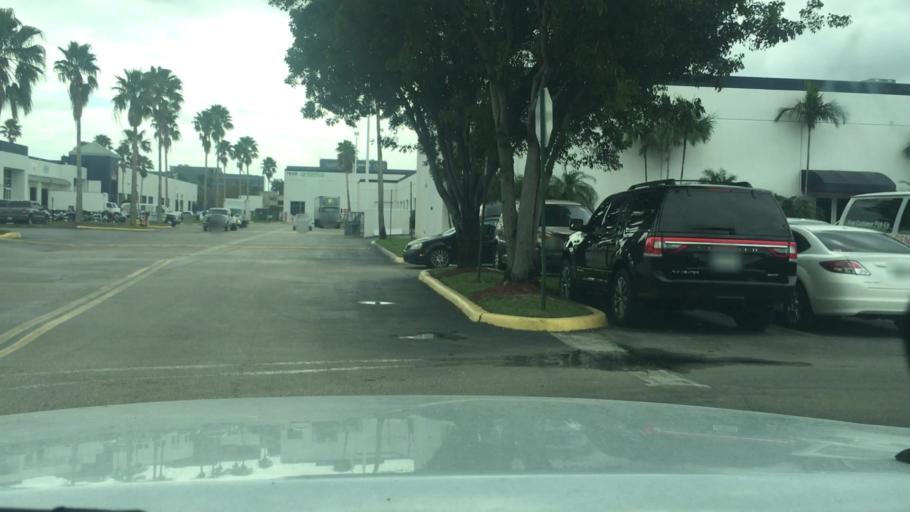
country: US
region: Florida
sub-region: Miami-Dade County
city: Virginia Gardens
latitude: 25.7958
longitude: -80.3202
